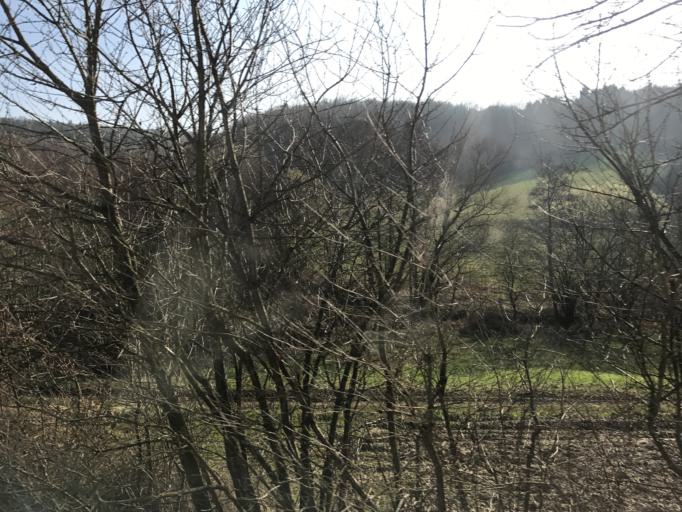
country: DE
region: Rheinland-Pfalz
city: Unkenbach
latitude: 49.7099
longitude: 7.7431
